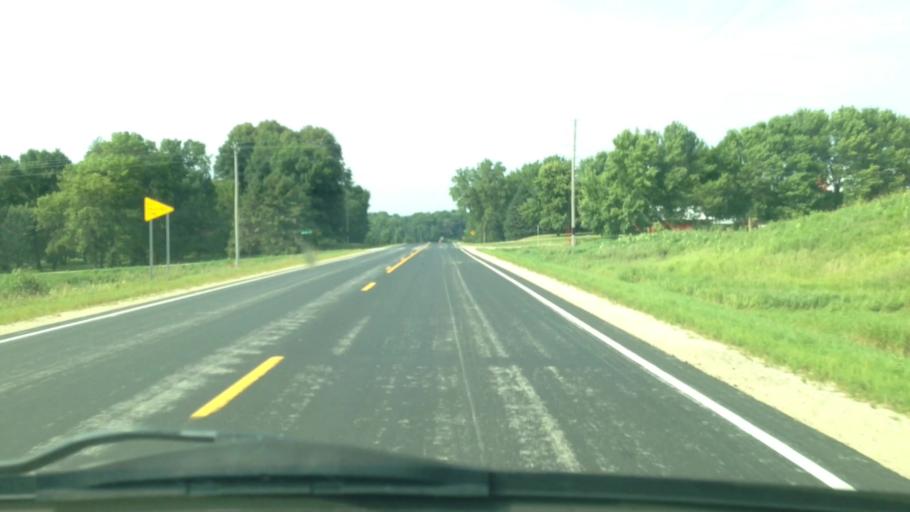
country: US
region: Minnesota
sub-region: Winona County
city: Lewiston
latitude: 43.9617
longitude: -91.9543
